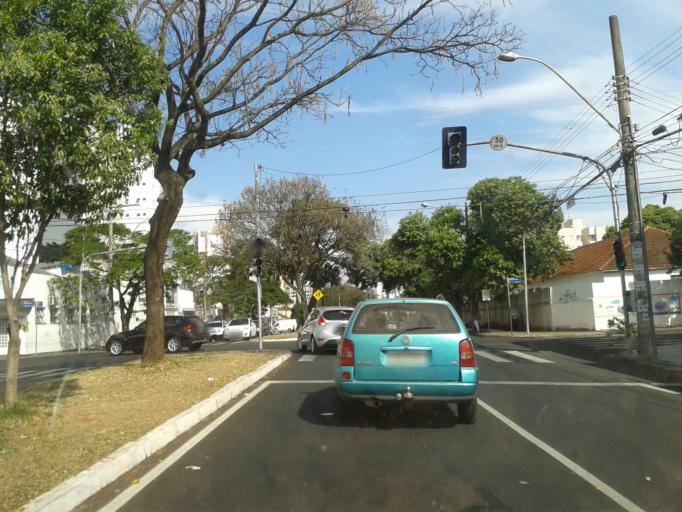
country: BR
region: Minas Gerais
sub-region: Uberlandia
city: Uberlandia
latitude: -18.9136
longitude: -48.2865
